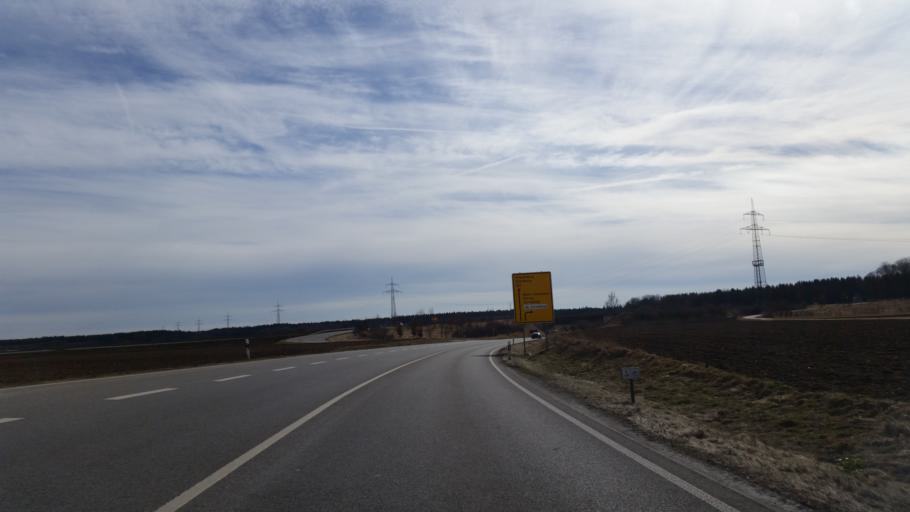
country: DE
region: Bavaria
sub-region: Upper Bavaria
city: Zorneding
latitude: 48.0829
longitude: 11.8094
